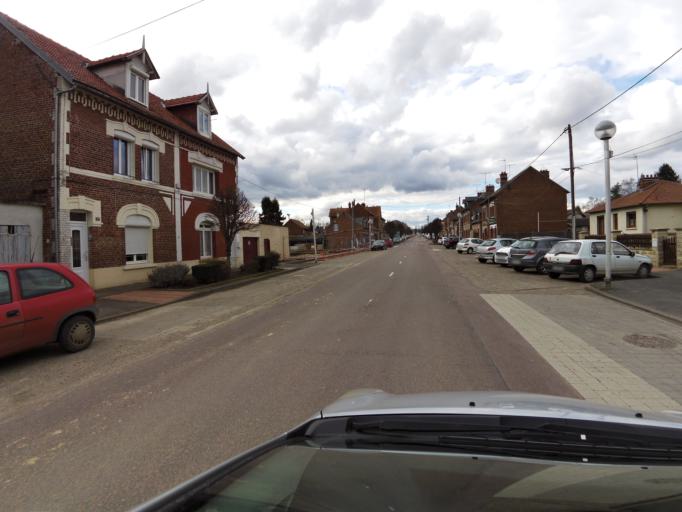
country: FR
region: Picardie
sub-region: Departement de la Somme
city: Roye
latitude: 49.6958
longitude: 2.7990
